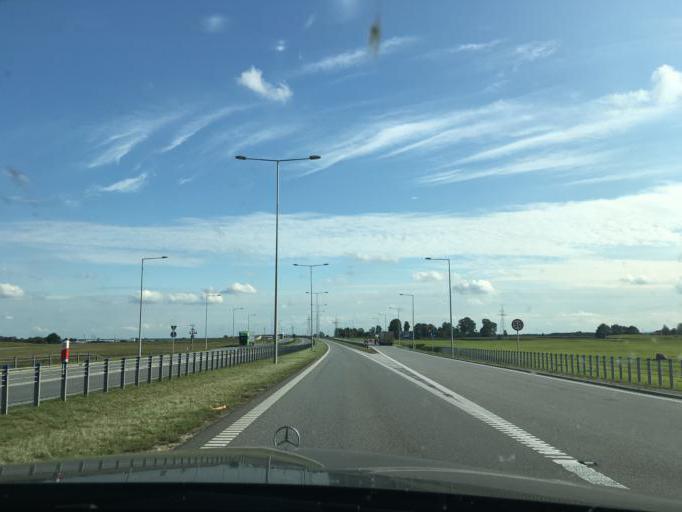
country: PL
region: Podlasie
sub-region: Powiat augustowski
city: Augustow
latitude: 53.8722
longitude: 22.8841
